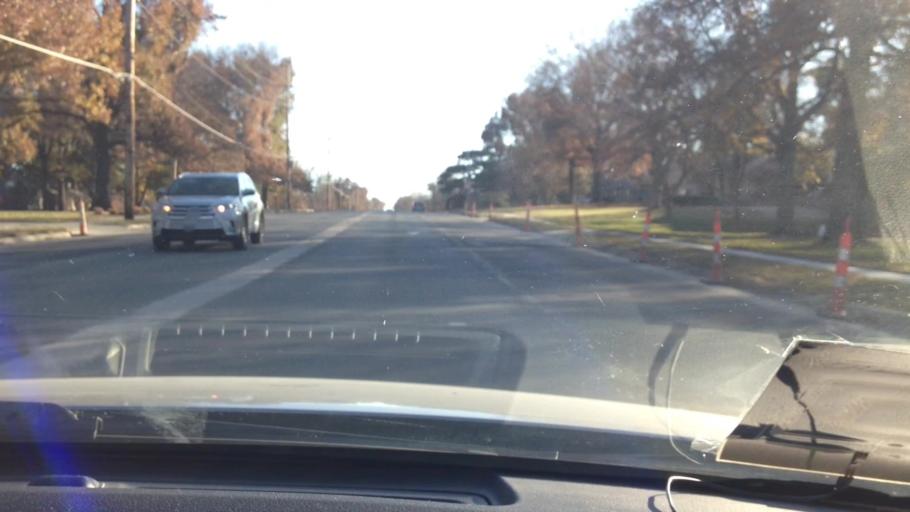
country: US
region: Kansas
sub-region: Johnson County
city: Leawood
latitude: 38.9705
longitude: -94.6303
